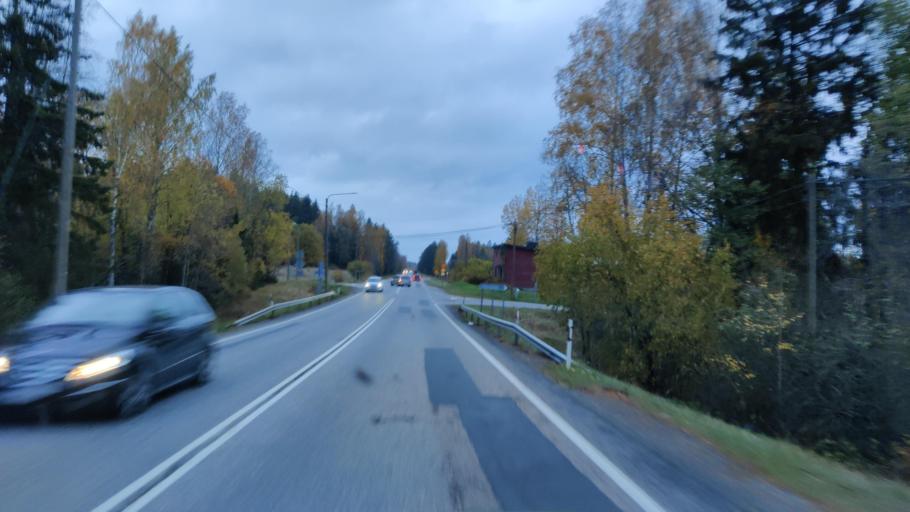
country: FI
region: Uusimaa
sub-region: Helsinki
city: Vihti
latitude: 60.3434
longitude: 24.1948
